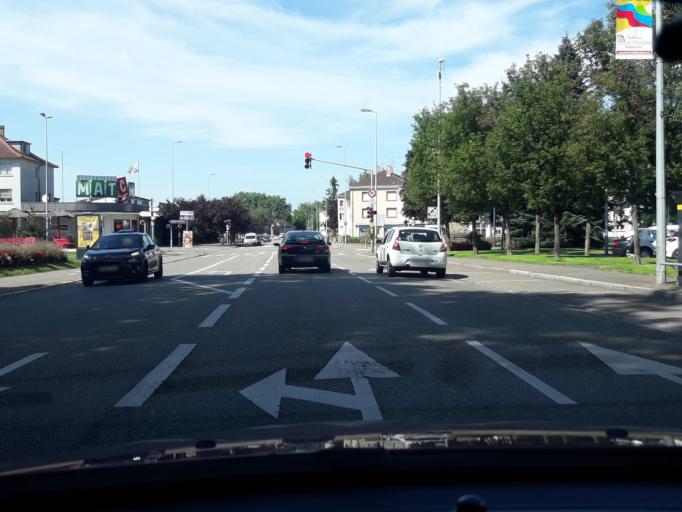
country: FR
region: Alsace
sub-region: Departement du Bas-Rhin
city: Haguenau
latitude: 48.8138
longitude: 7.7840
